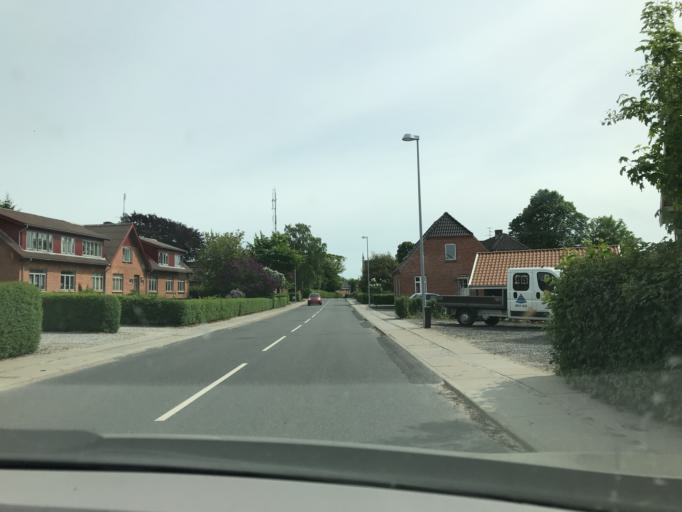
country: DK
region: Central Jutland
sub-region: Norddjurs Kommune
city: Allingabro
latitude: 56.5047
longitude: 10.3353
